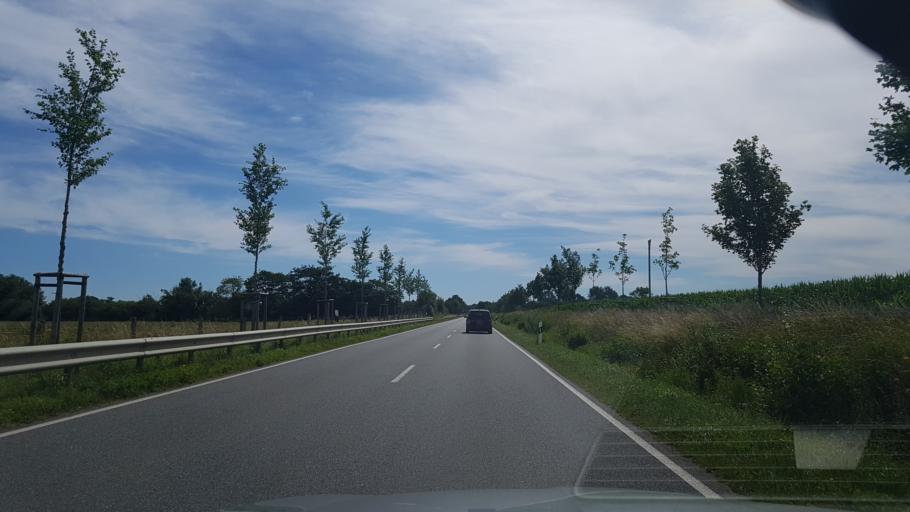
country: DE
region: Schleswig-Holstein
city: Wallsbull
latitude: 54.7979
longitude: 9.2818
